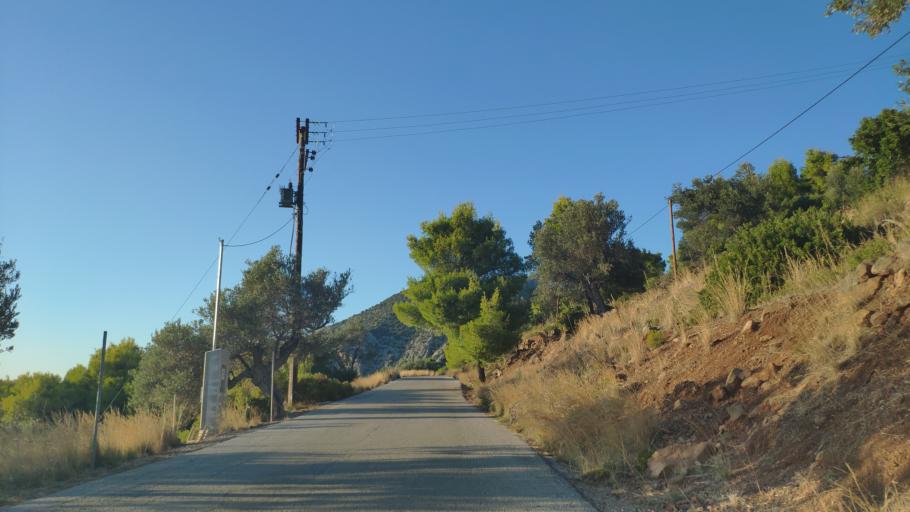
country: GR
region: Attica
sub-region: Nomos Piraios
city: Megalochori
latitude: 37.6031
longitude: 23.3307
